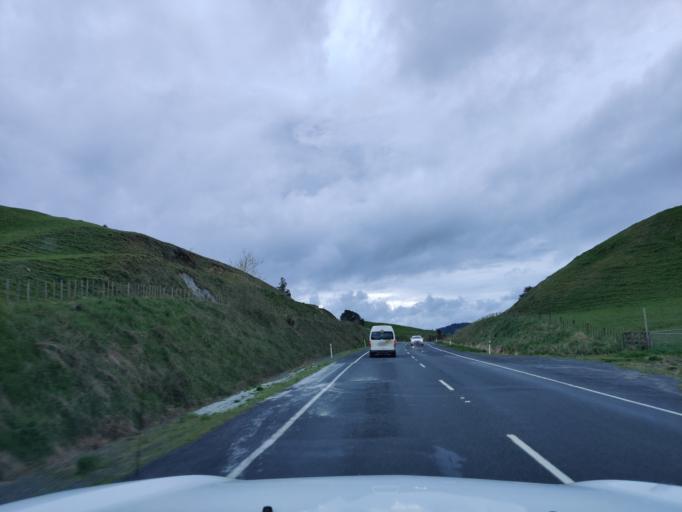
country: NZ
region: Waikato
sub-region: Otorohanga District
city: Otorohanga
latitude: -38.4677
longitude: 175.1690
